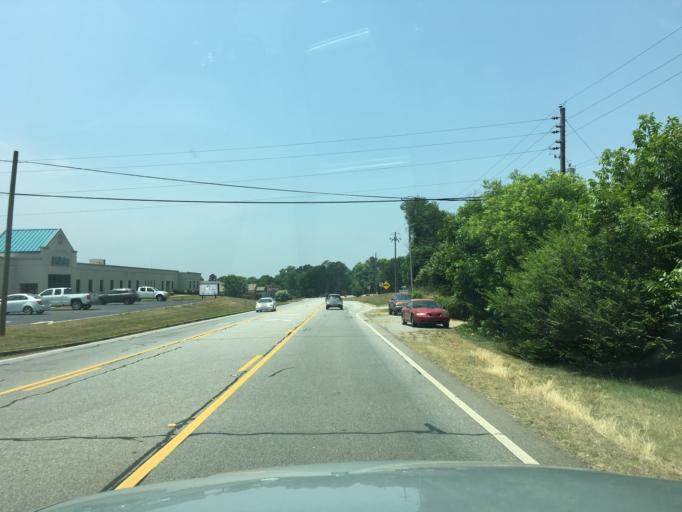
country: US
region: Georgia
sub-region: Hart County
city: Royston
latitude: 34.2841
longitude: -83.1500
